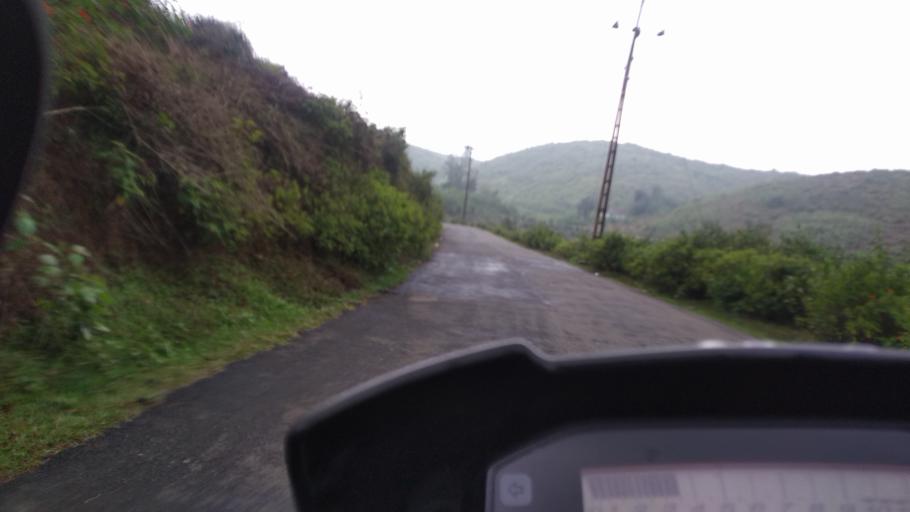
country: IN
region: Kerala
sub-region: Kottayam
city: Erattupetta
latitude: 9.6320
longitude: 76.9449
